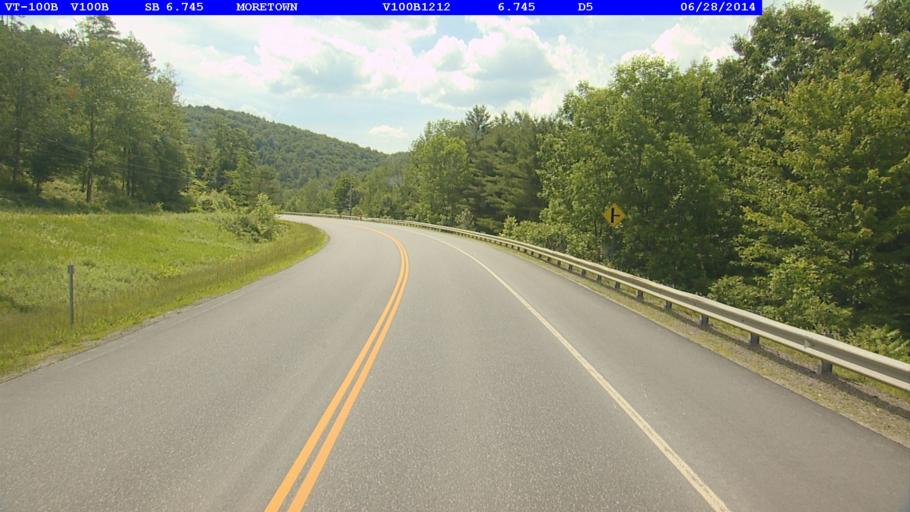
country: US
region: Vermont
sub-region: Washington County
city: Waterbury
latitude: 44.2969
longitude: -72.6989
